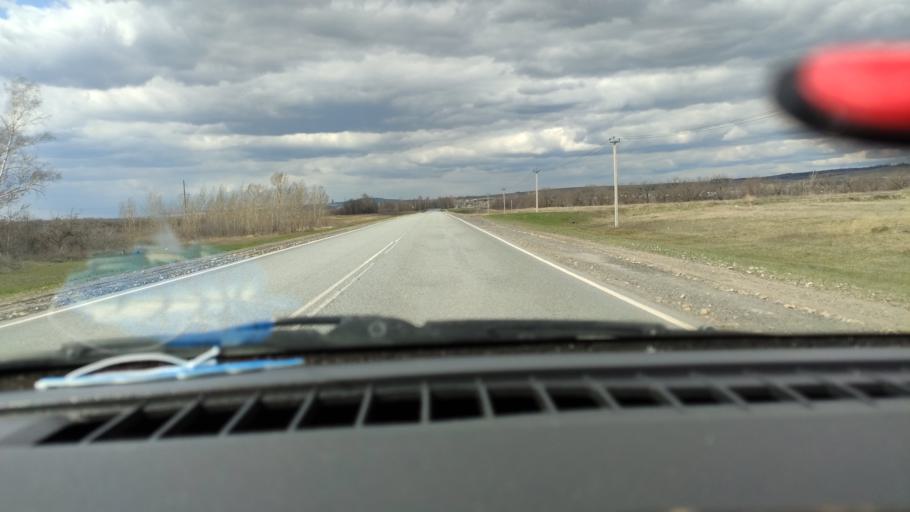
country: RU
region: Saratov
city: Tersa
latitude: 52.0860
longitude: 47.6170
